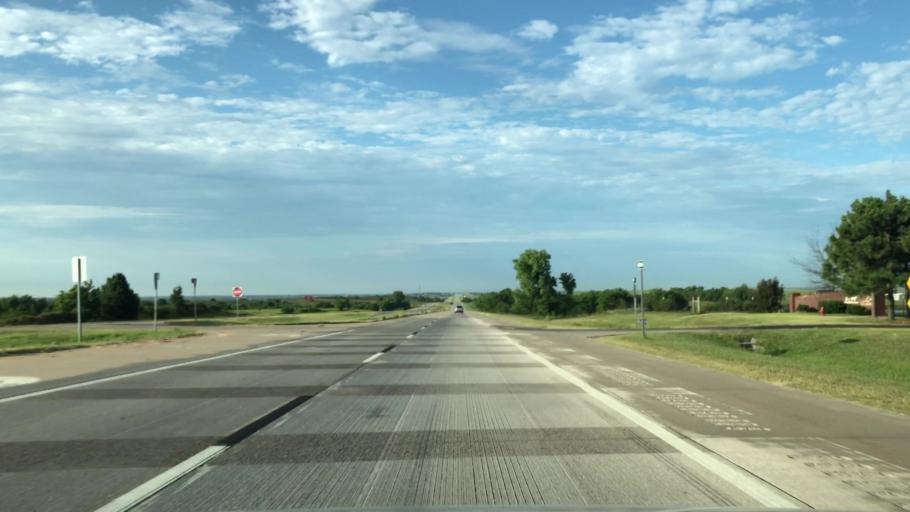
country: US
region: Oklahoma
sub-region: Osage County
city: Skiatook
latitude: 36.4168
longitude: -95.9207
